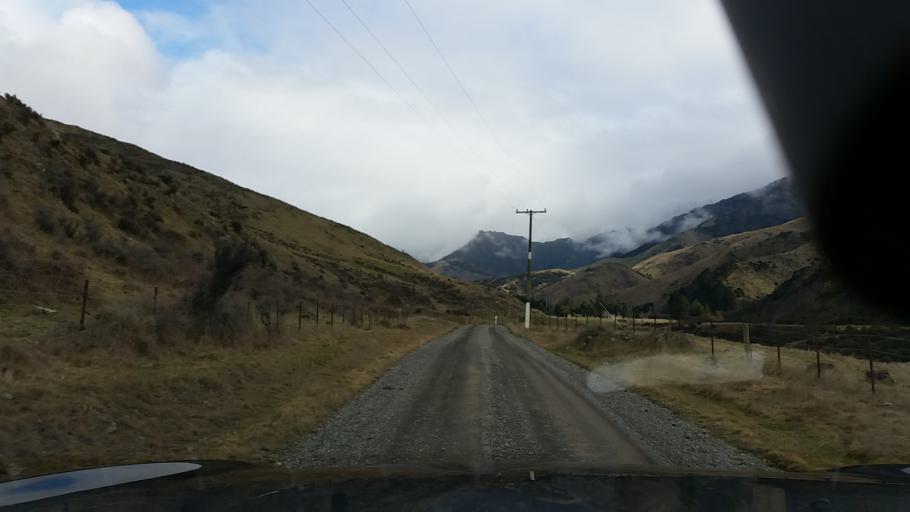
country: NZ
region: Tasman
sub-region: Tasman District
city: Richmond
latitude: -41.7318
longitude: 173.4370
